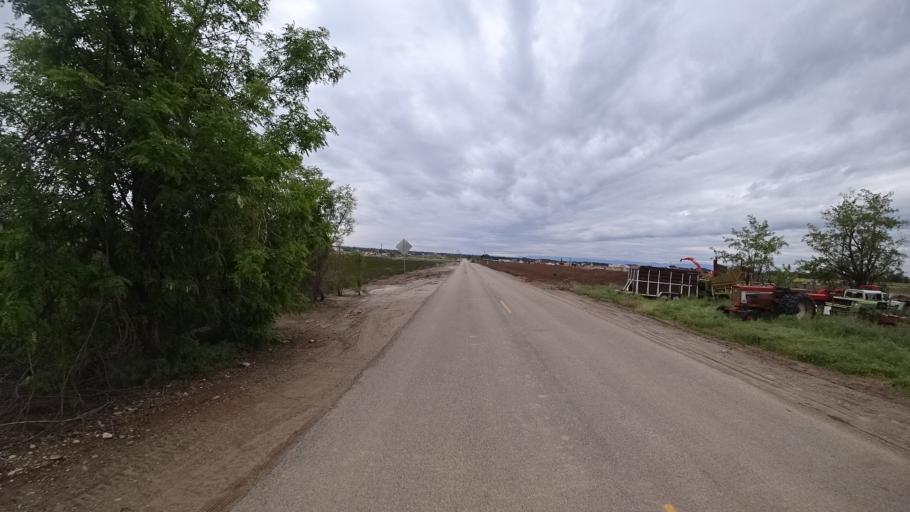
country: US
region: Idaho
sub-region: Ada County
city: Eagle
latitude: 43.7198
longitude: -116.4234
